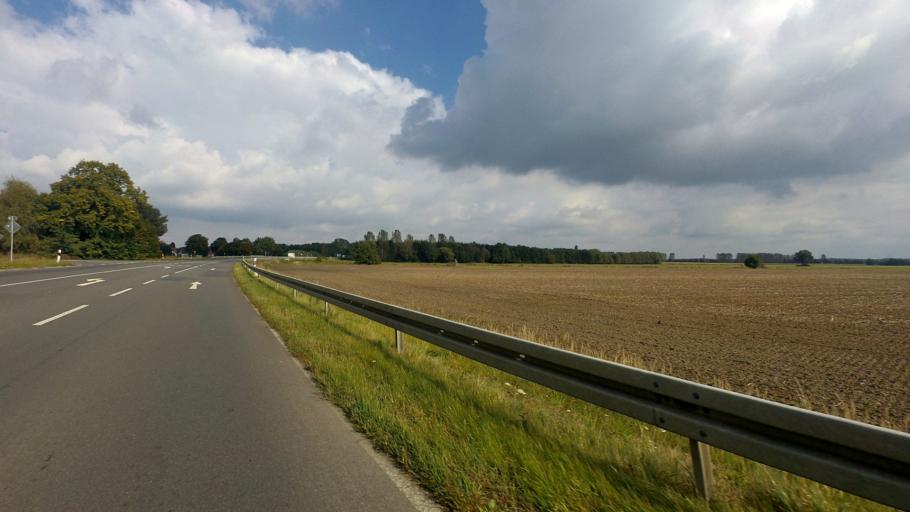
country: DE
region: Brandenburg
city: Herzberg
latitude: 51.7477
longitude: 13.2053
